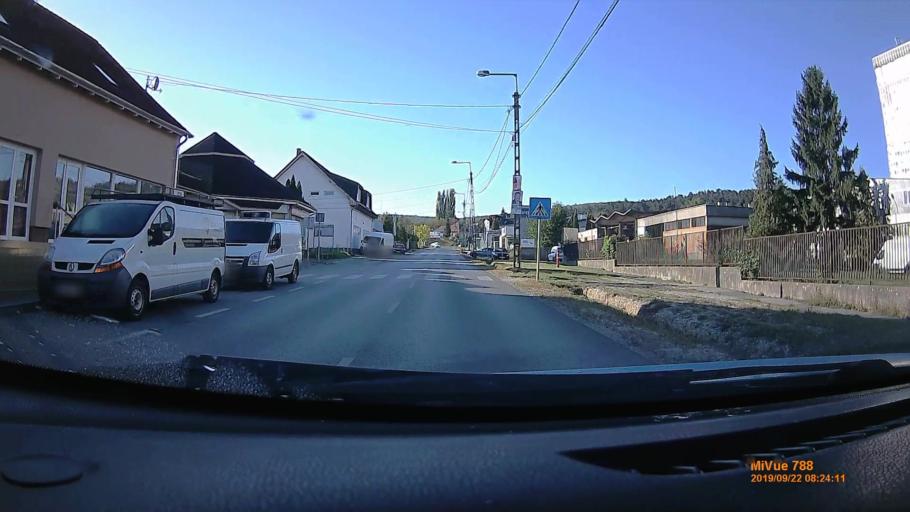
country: HU
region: Borsod-Abauj-Zemplen
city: Miskolc
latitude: 48.0924
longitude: 20.7113
